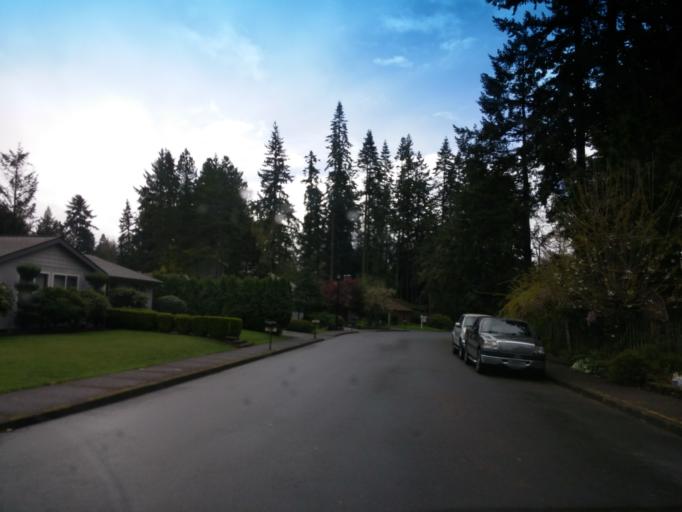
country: US
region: Oregon
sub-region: Washington County
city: Aloha
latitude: 45.5026
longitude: -122.8546
